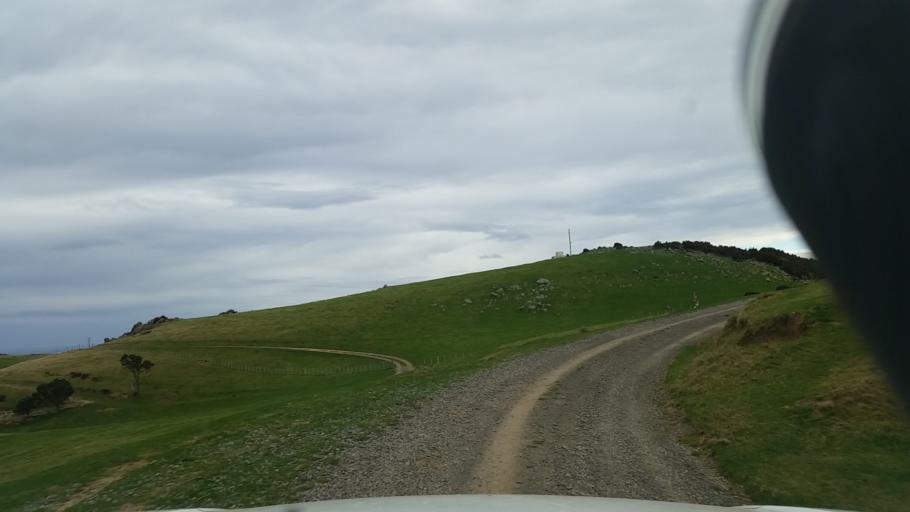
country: NZ
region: Canterbury
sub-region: Christchurch City
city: Christchurch
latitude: -43.8571
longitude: 173.0203
